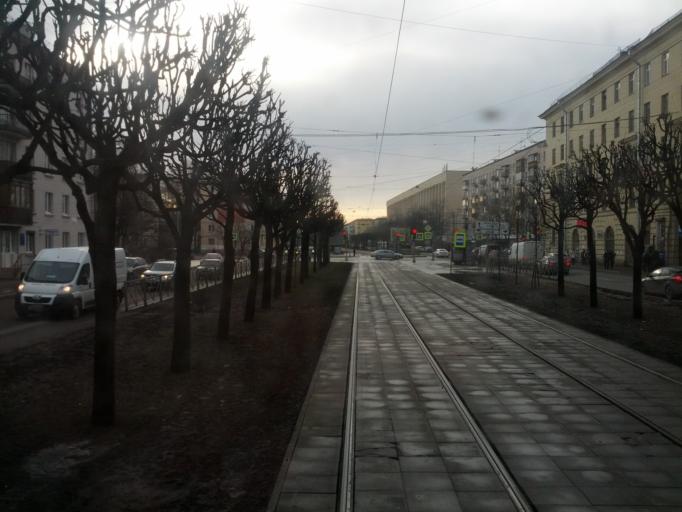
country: RU
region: St.-Petersburg
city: Centralniy
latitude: 59.9256
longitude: 30.4153
